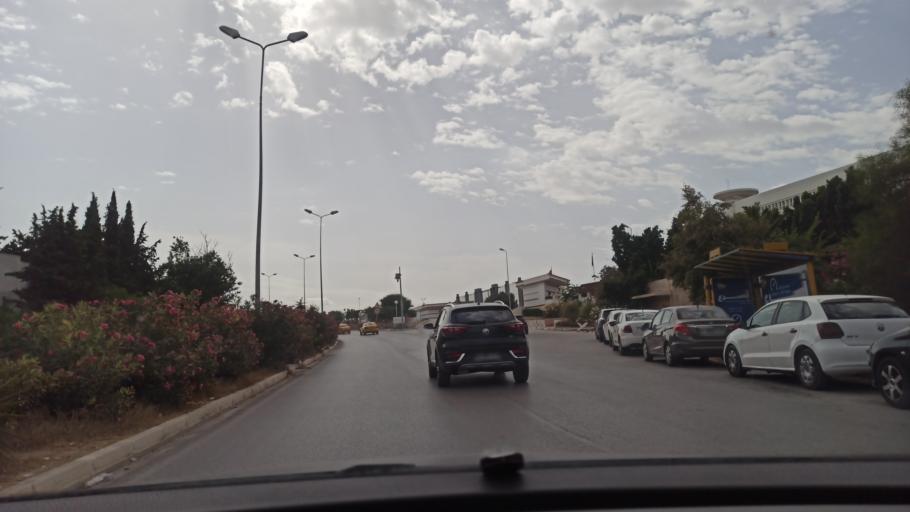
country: TN
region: Tunis
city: Tunis
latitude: 36.8303
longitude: 10.1582
